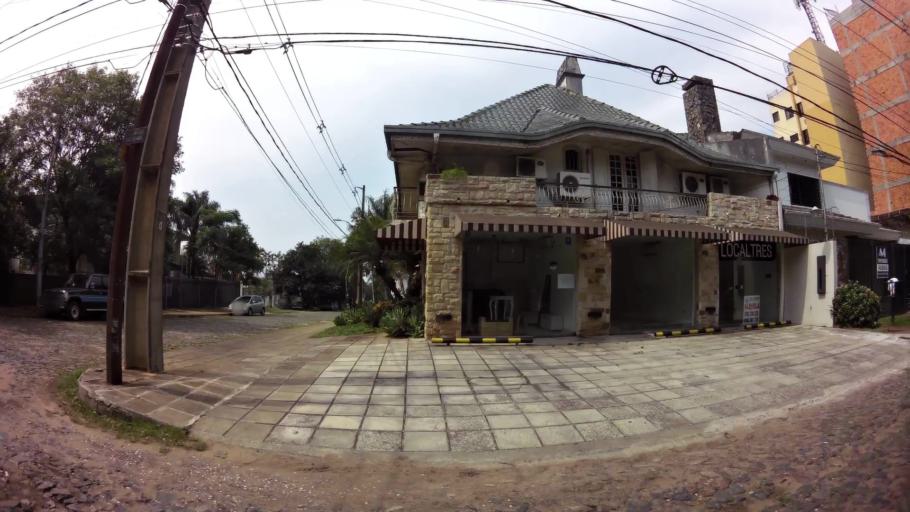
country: PY
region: Asuncion
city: Asuncion
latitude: -25.2779
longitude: -57.5703
